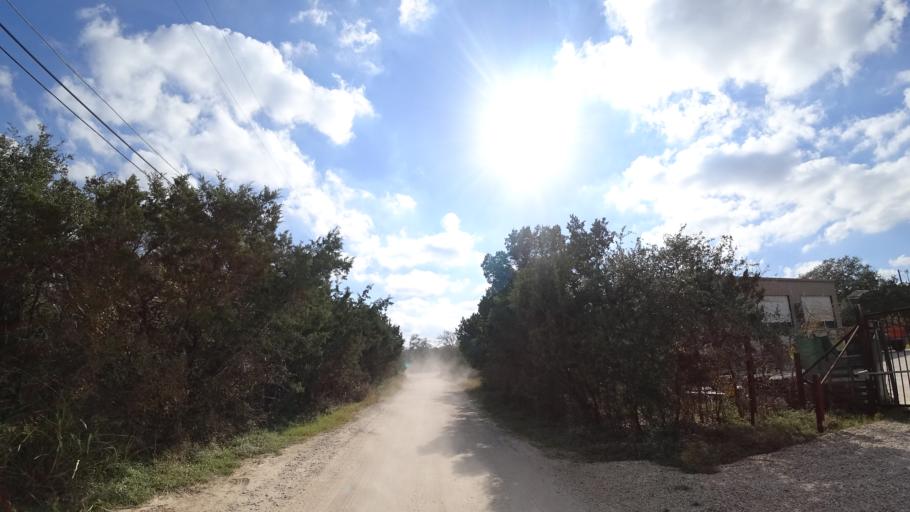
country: US
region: Texas
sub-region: Travis County
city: Shady Hollow
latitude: 30.1747
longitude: -97.8636
